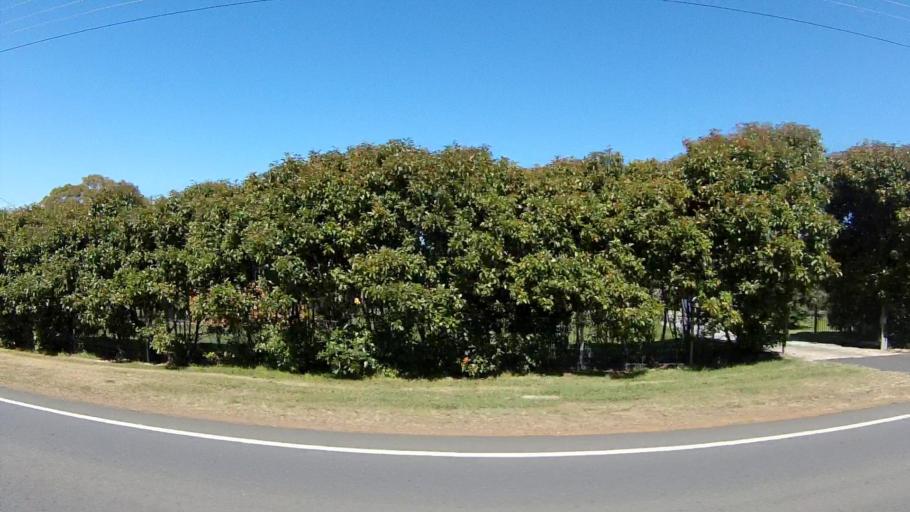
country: AU
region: Tasmania
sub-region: Sorell
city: Sorell
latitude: -42.5522
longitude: 147.8770
